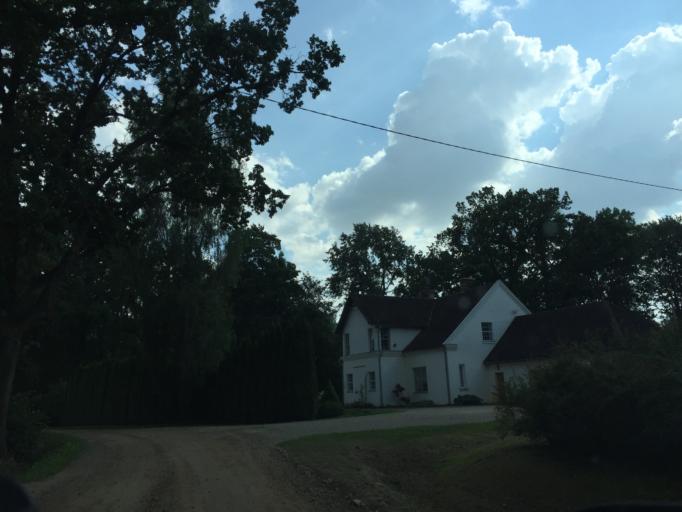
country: LV
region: Jelgava
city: Jelgava
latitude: 56.5055
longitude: 23.7551
